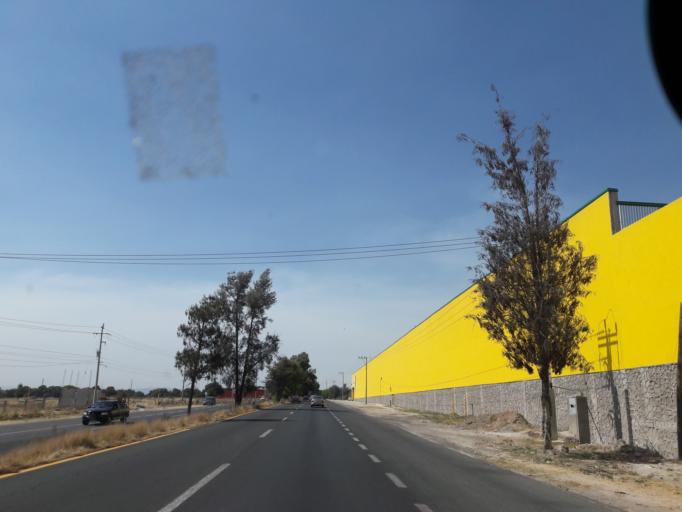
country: MX
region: Tlaxcala
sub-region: Mazatecochco de Jose Maria Morelos
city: Mazatecochco
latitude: 19.1876
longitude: -98.1937
